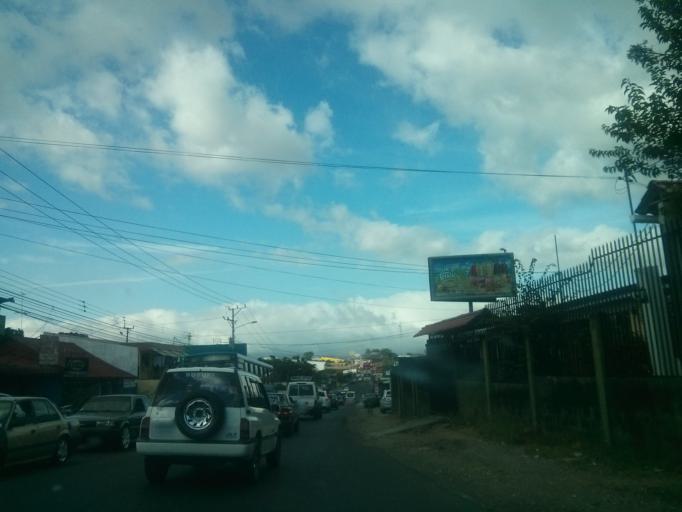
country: CR
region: San Jose
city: San Rafael Arriba
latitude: 9.8863
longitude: -84.0655
